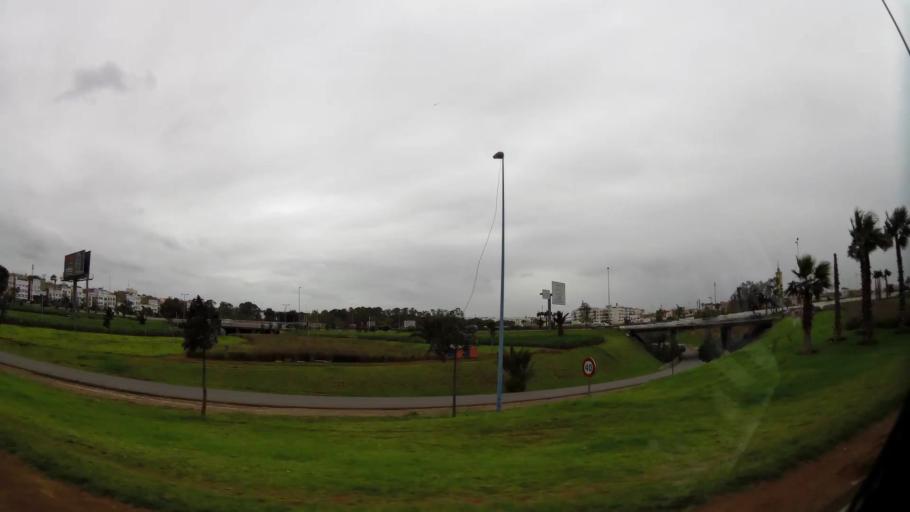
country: MA
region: Grand Casablanca
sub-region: Casablanca
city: Casablanca
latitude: 33.5689
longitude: -7.5752
